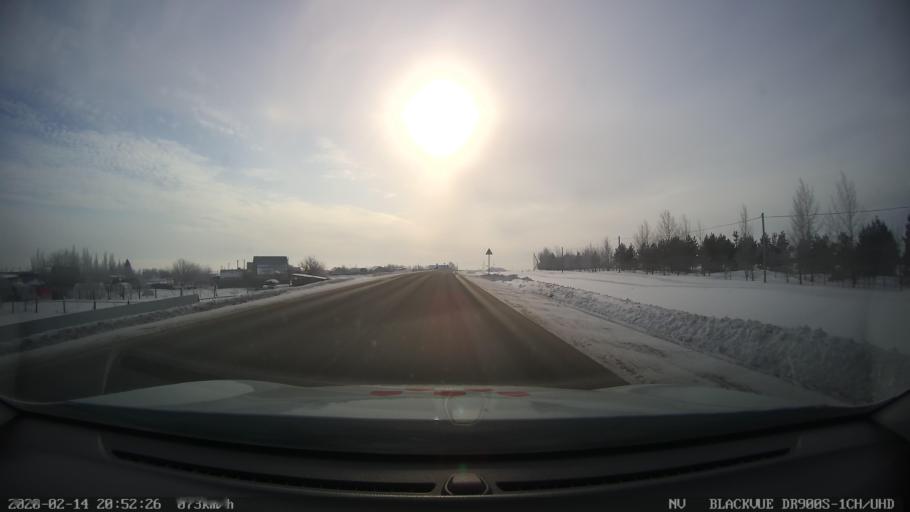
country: RU
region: Tatarstan
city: Kuybyshevskiy Zaton
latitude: 55.2045
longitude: 49.2489
